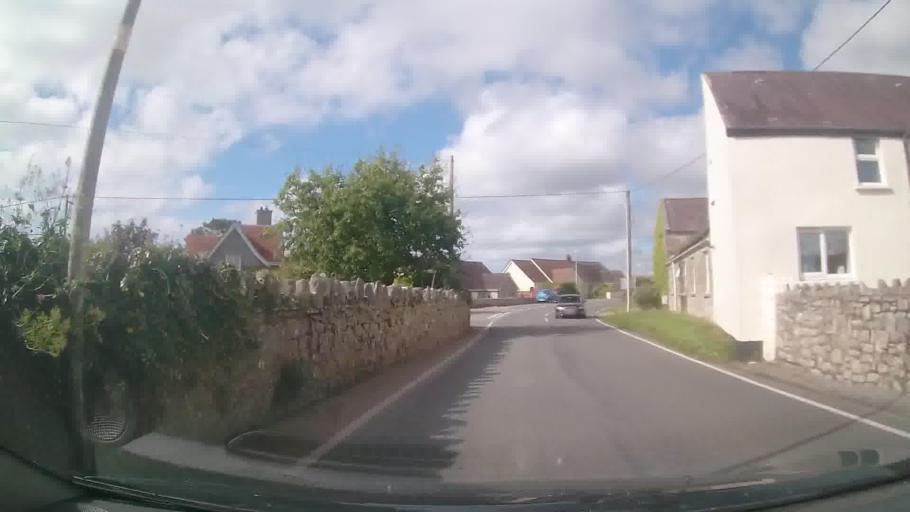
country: GB
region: Wales
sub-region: Pembrokeshire
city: Manorbier
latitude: 51.6510
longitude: -4.7681
